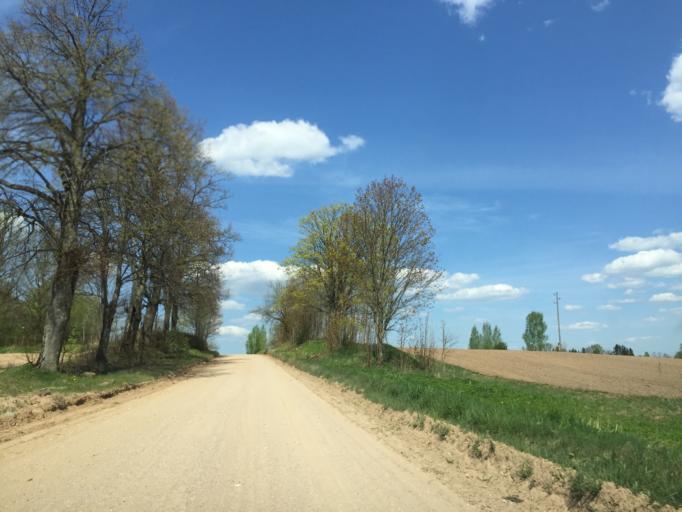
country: LV
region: Krimulda
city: Ragana
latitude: 57.3475
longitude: 24.6516
